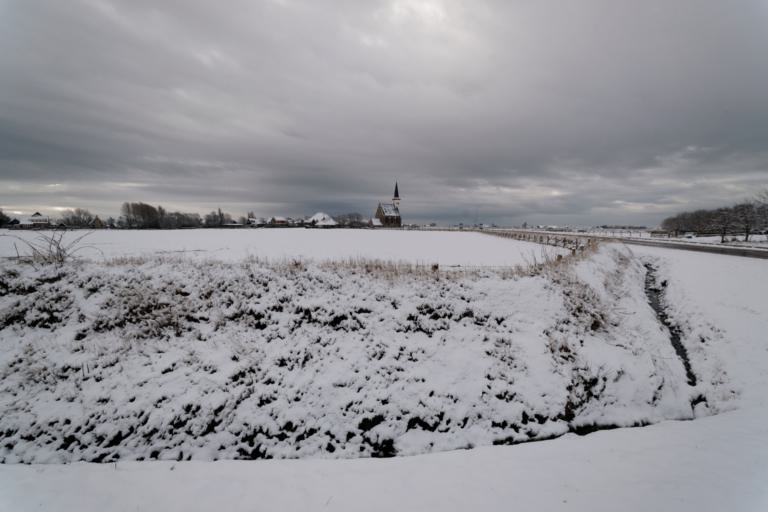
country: NL
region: North Holland
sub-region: Gemeente Texel
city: Den Burg
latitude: 53.0285
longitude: 4.7530
